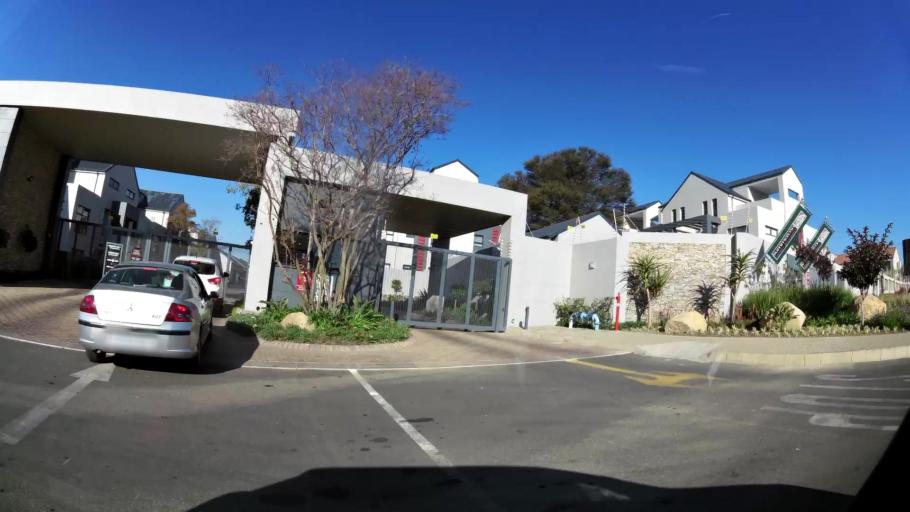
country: ZA
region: Gauteng
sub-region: City of Johannesburg Metropolitan Municipality
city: Diepsloot
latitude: -26.0243
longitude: 28.0358
